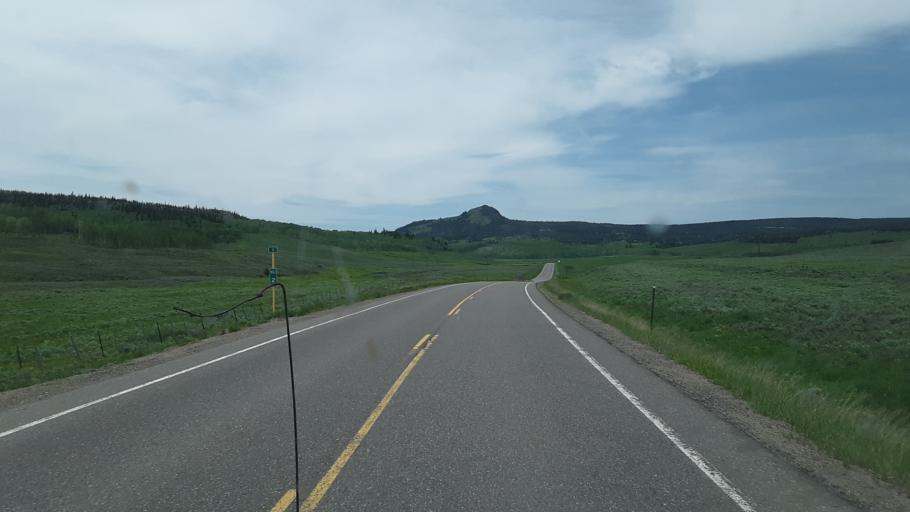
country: US
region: Colorado
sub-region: Routt County
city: Steamboat Springs
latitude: 40.3979
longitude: -106.5519
